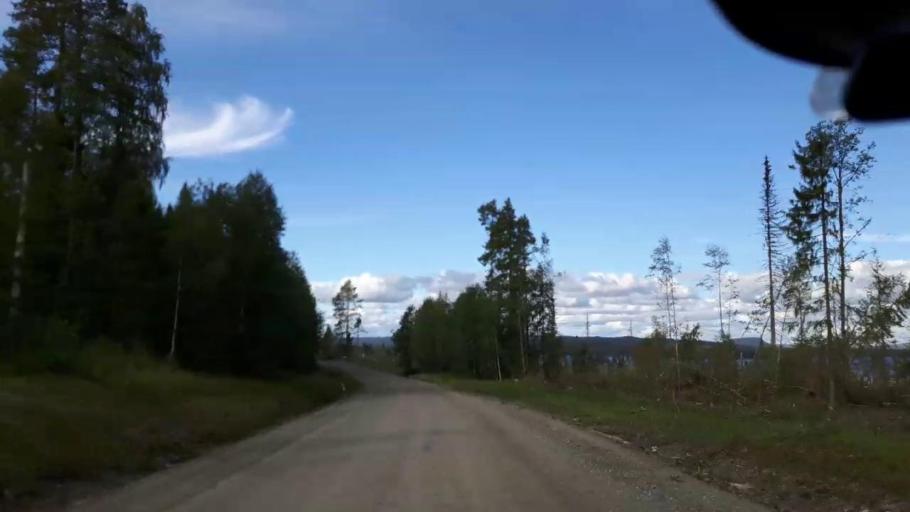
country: SE
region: Jaemtland
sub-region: Ragunda Kommun
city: Hammarstrand
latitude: 63.1364
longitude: 15.9447
